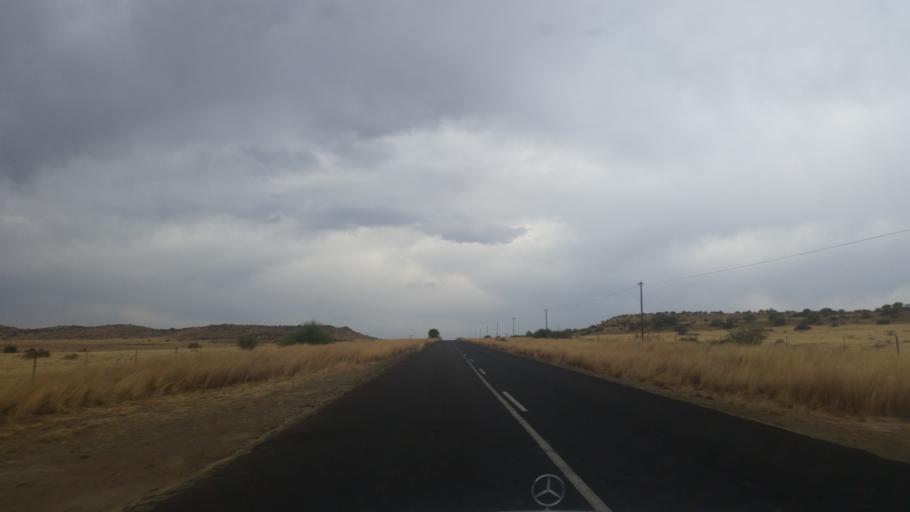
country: ZA
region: Orange Free State
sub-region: Xhariep District Municipality
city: Trompsburg
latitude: -30.4231
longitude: 26.1520
